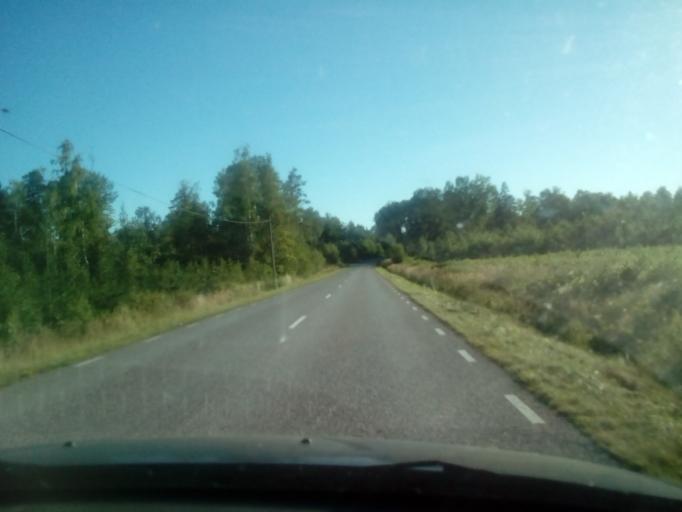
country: SE
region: Kalmar
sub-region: Vasterviks Kommun
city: Ankarsrum
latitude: 57.7847
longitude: 16.2960
